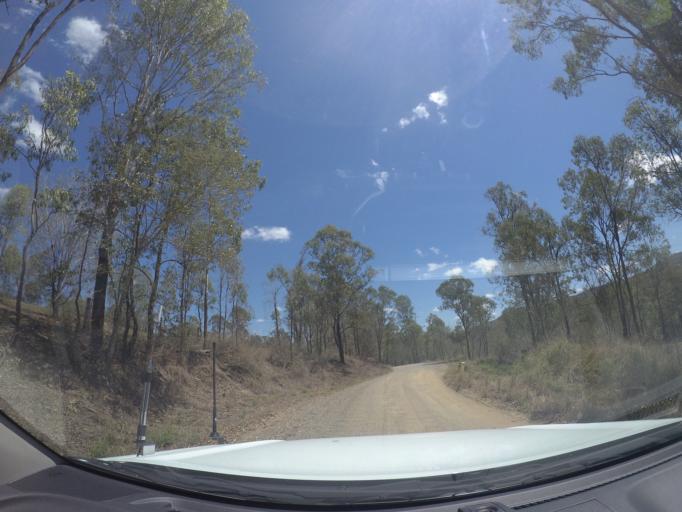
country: AU
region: Queensland
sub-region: Logan
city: North Maclean
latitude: -27.8343
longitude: 152.8690
